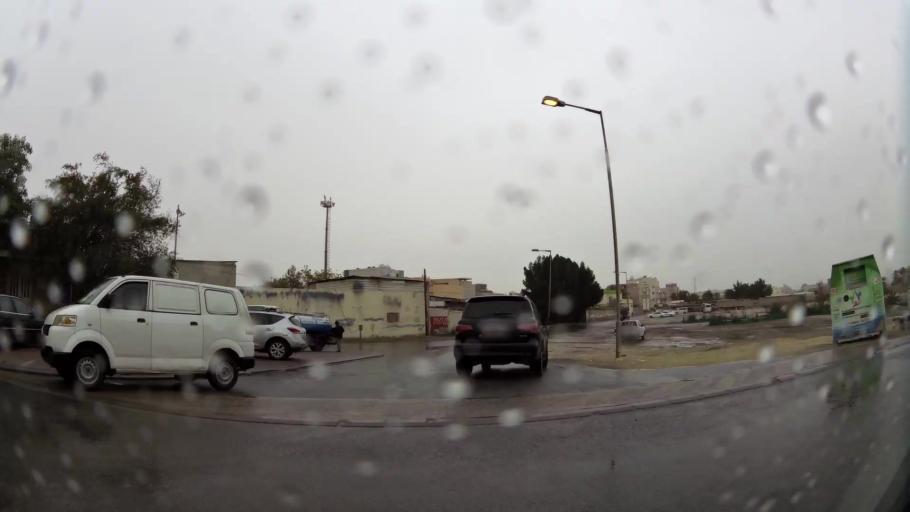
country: BH
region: Northern
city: Madinat `Isa
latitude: 26.1830
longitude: 50.5532
